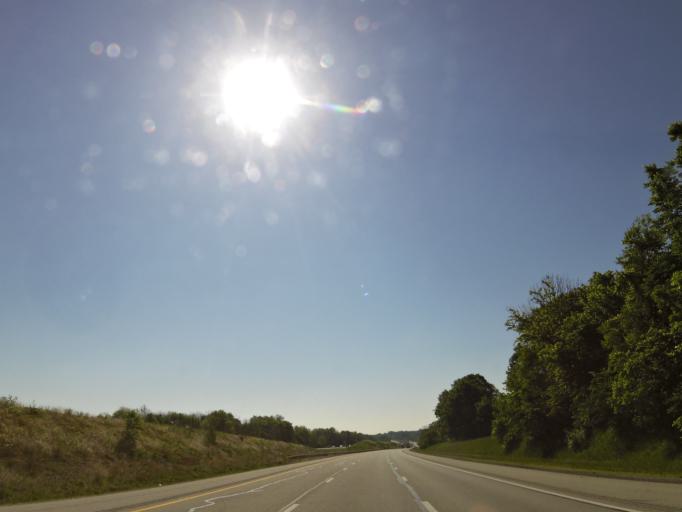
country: US
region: Kentucky
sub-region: Shelby County
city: Shelbyville
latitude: 38.1630
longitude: -85.1052
